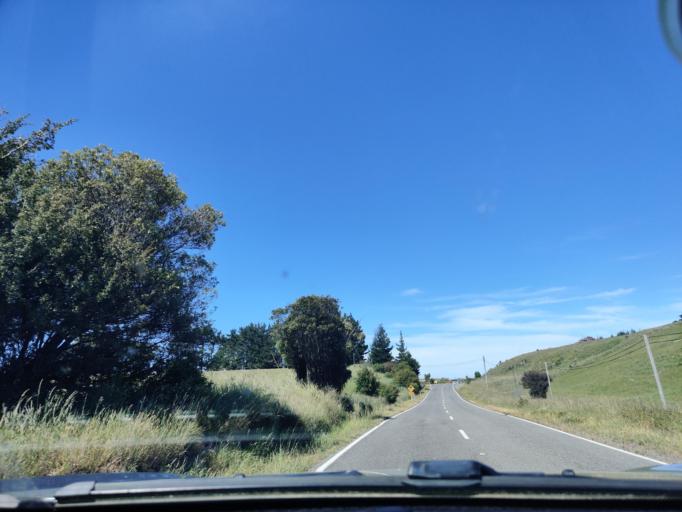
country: NZ
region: Wellington
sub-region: Upper Hutt City
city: Upper Hutt
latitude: -41.3634
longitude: 175.1998
